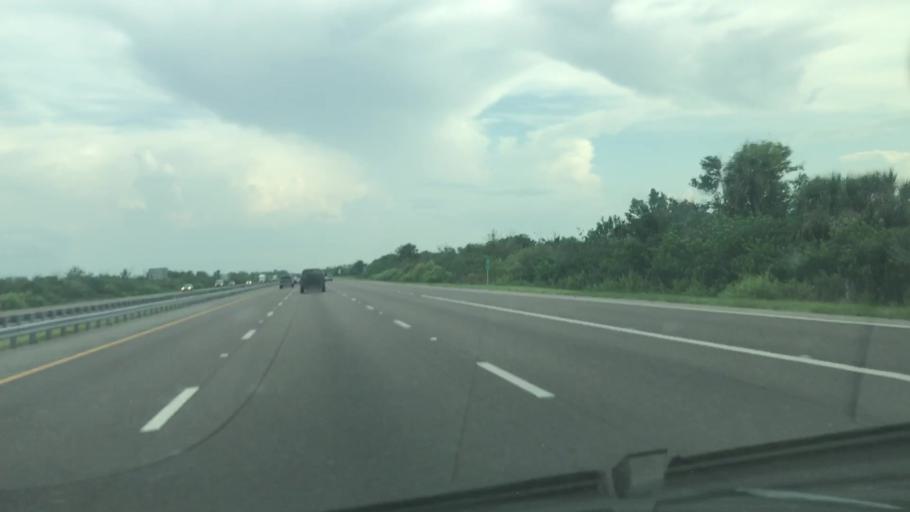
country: US
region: Florida
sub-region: Brevard County
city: Titusville
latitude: 28.5494
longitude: -80.8541
